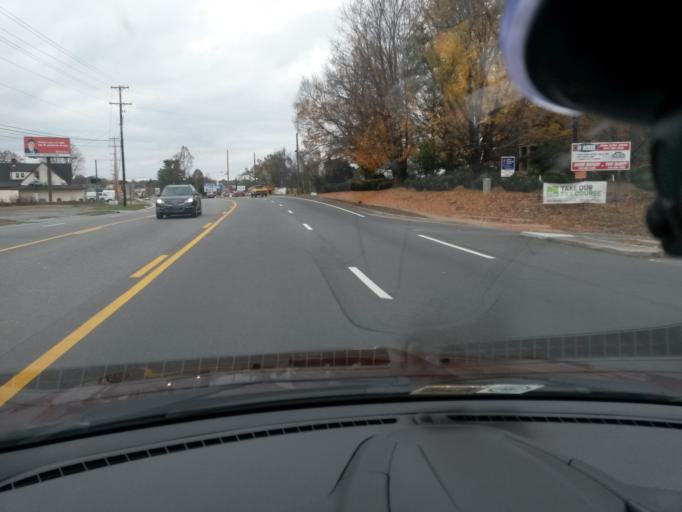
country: US
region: Virginia
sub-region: Amherst County
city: Madison Heights
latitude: 37.4629
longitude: -79.1188
